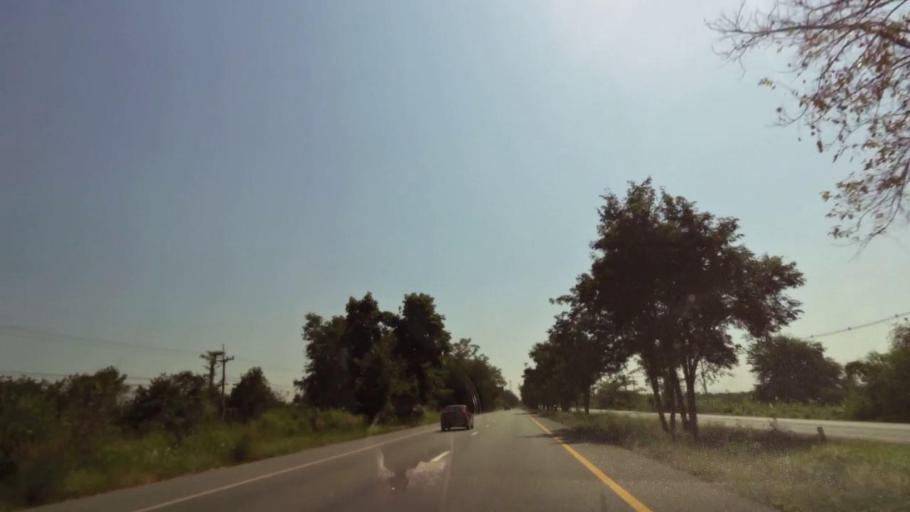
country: TH
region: Nakhon Sawan
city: Kao Liao
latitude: 15.8823
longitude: 100.1155
